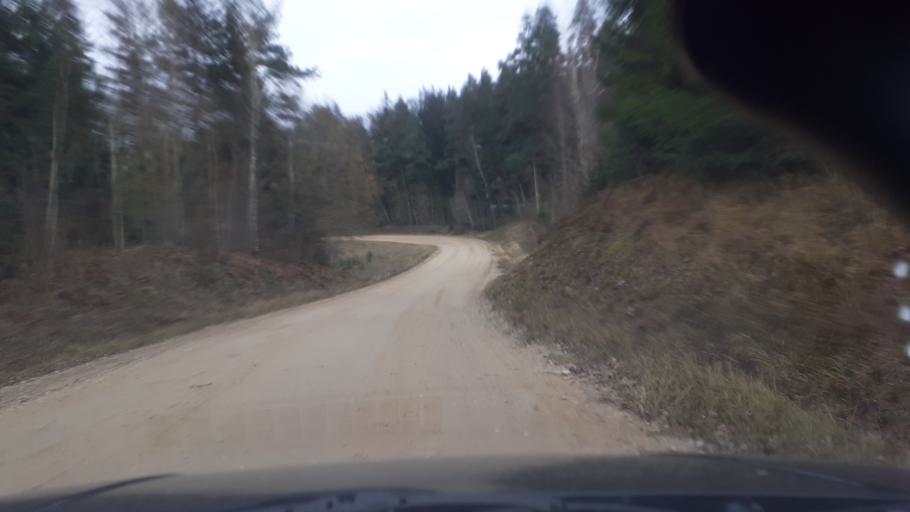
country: LV
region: Alsunga
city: Alsunga
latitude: 56.9842
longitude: 21.6696
